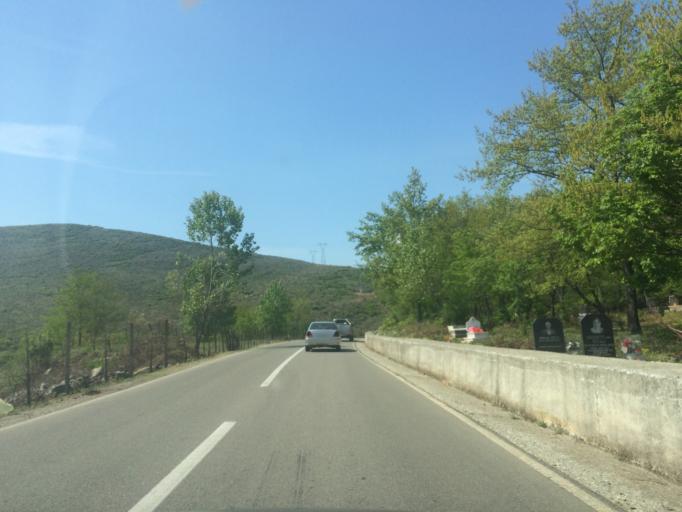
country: AL
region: Kukes
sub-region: Rrethi i Tropojes
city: Llugaj
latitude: 42.3839
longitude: 20.1546
